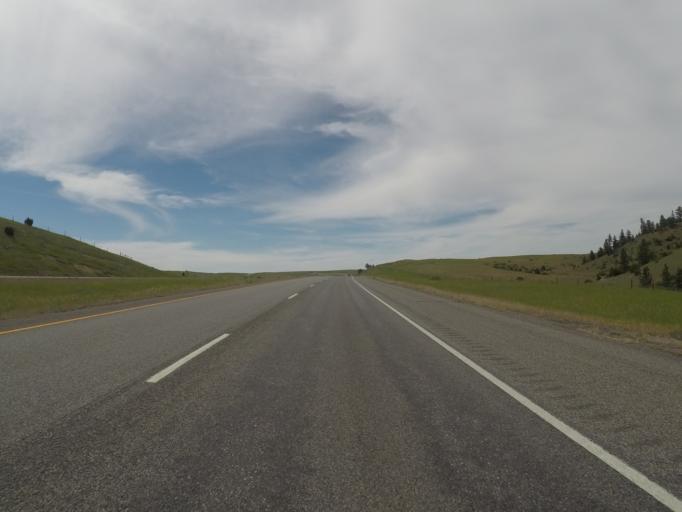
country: US
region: Montana
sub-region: Stillwater County
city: Columbus
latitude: 45.6219
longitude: -109.1879
